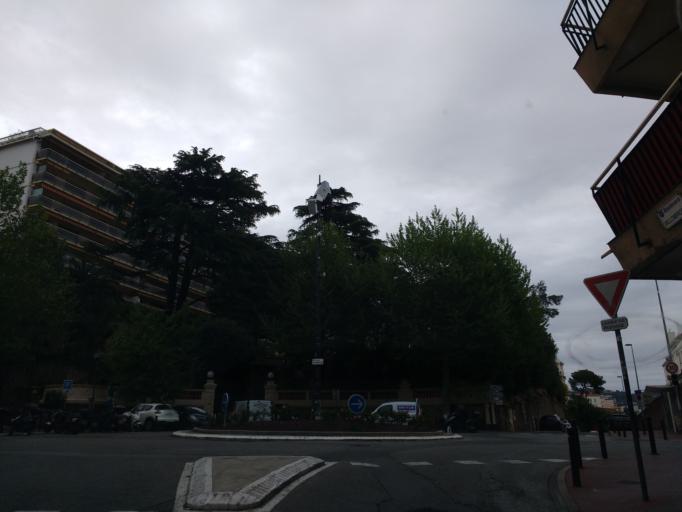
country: FR
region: Provence-Alpes-Cote d'Azur
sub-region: Departement des Alpes-Maritimes
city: Cannes
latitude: 43.5536
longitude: 7.0078
